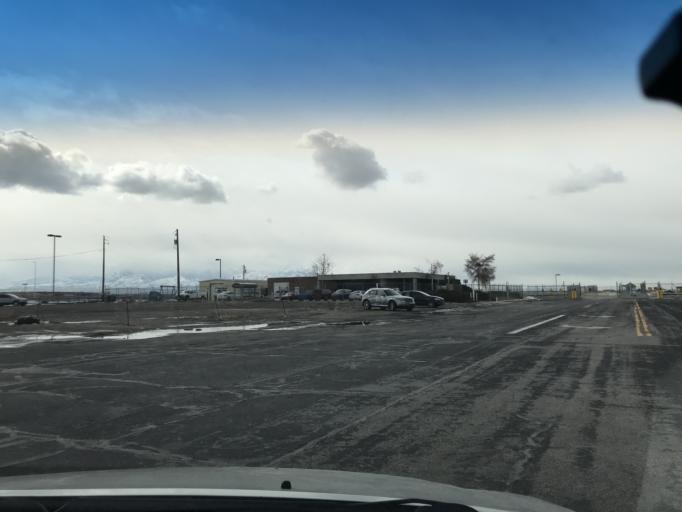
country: US
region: Utah
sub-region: Salt Lake County
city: Salt Lake City
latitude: 40.7715
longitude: -111.9581
